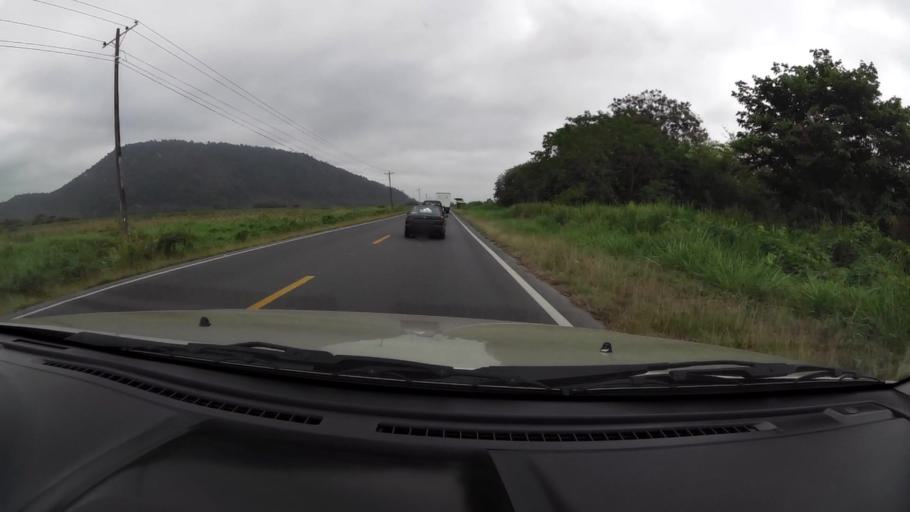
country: EC
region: Guayas
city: Naranjal
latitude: -2.4302
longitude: -79.6259
